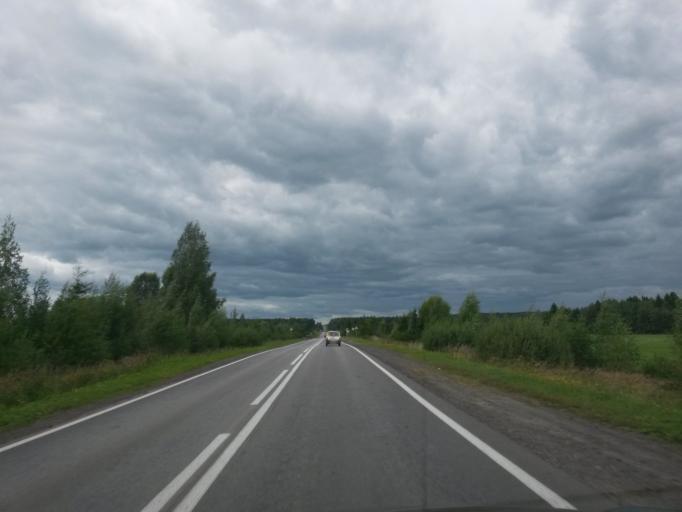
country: RU
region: Jaroslavl
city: Konstantinovskiy
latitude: 57.8096
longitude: 39.7363
